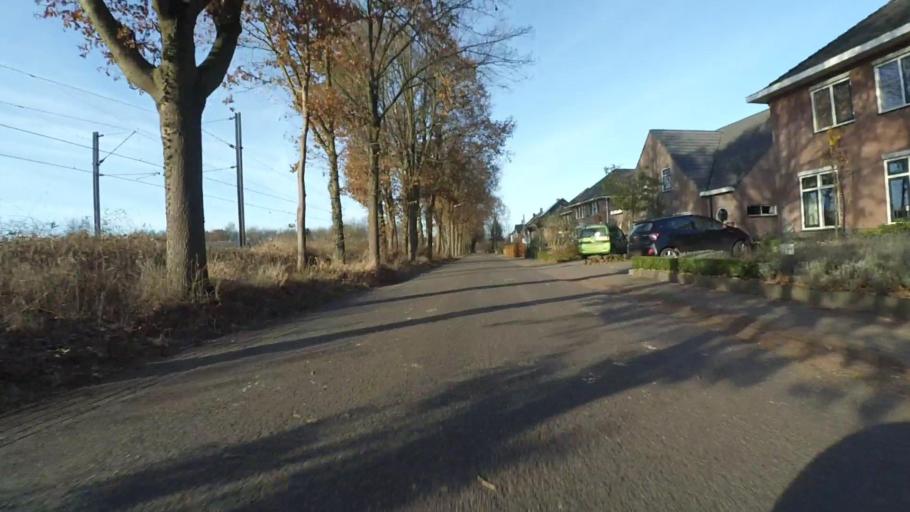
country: NL
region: Utrecht
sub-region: Gemeente Utrechtse Heuvelrug
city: Overberg
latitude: 52.0387
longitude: 5.4978
